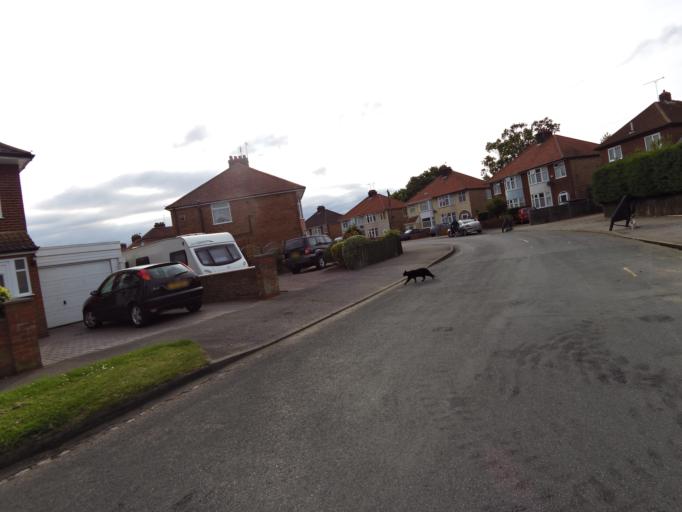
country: GB
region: England
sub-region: Suffolk
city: Ipswich
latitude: 52.0362
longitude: 1.1886
